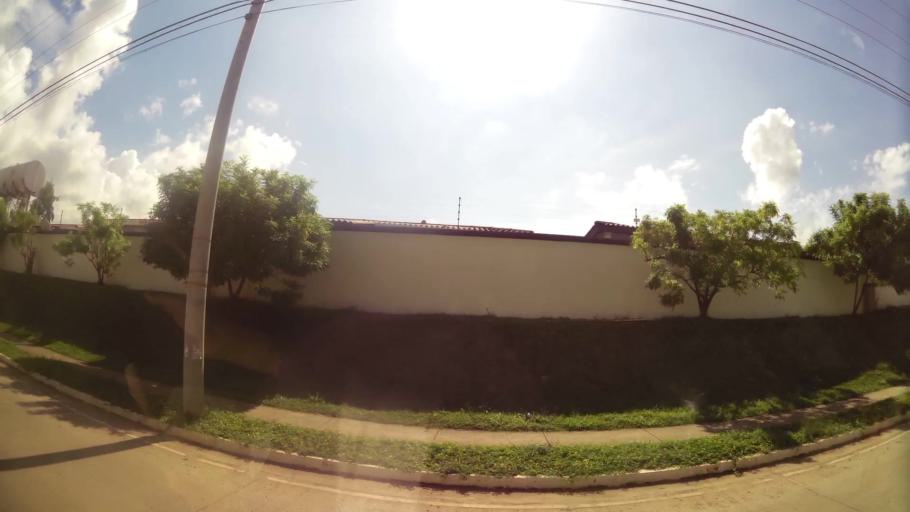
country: PA
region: Panama
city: Nuevo Arraijan
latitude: 8.9025
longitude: -79.7454
